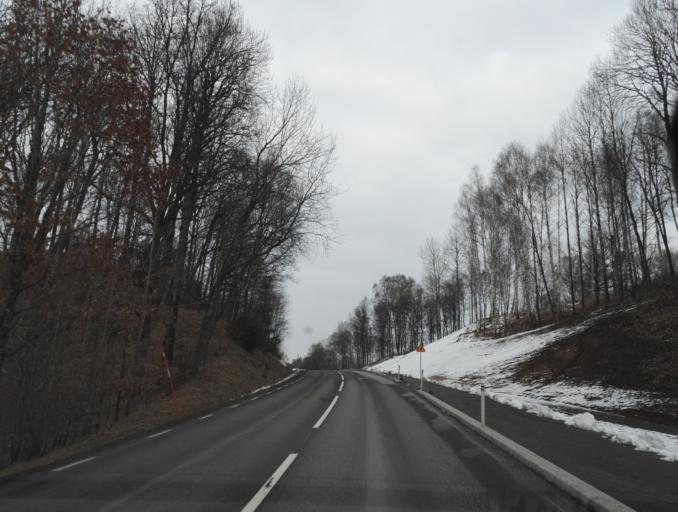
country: SE
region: Vaestra Goetaland
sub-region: Bollebygds Kommun
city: Bollebygd
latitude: 57.6908
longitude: 12.5698
